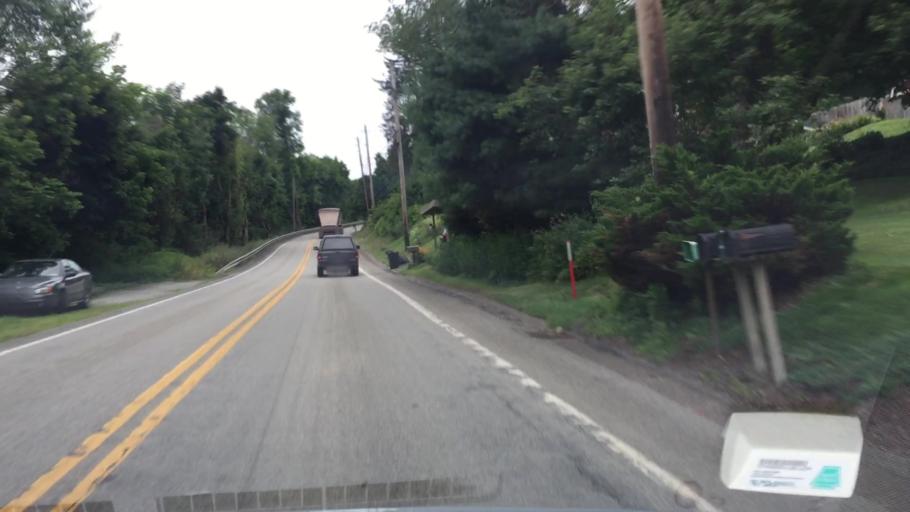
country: US
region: Pennsylvania
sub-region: Allegheny County
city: Curtisville
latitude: 40.6564
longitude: -79.8371
